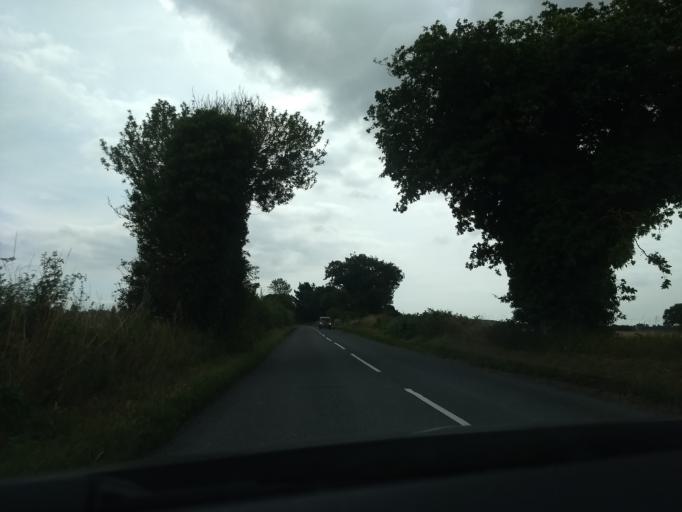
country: GB
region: England
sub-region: Suffolk
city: Ipswich
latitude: 51.9930
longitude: 1.1944
